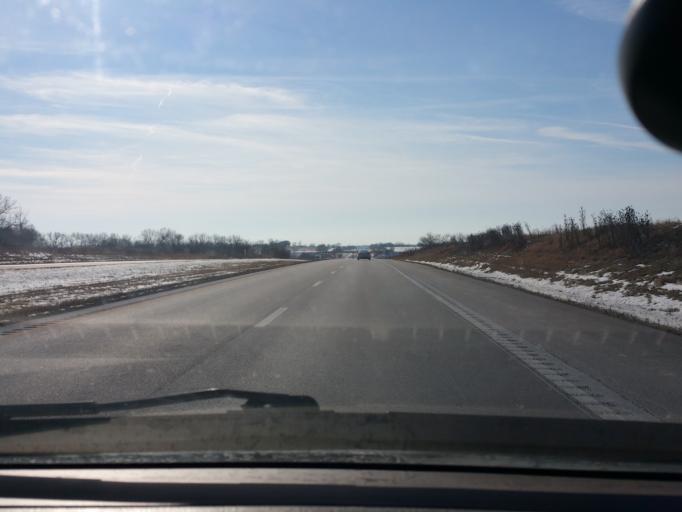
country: US
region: Missouri
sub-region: Clinton County
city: Cameron
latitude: 39.8103
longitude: -94.1961
